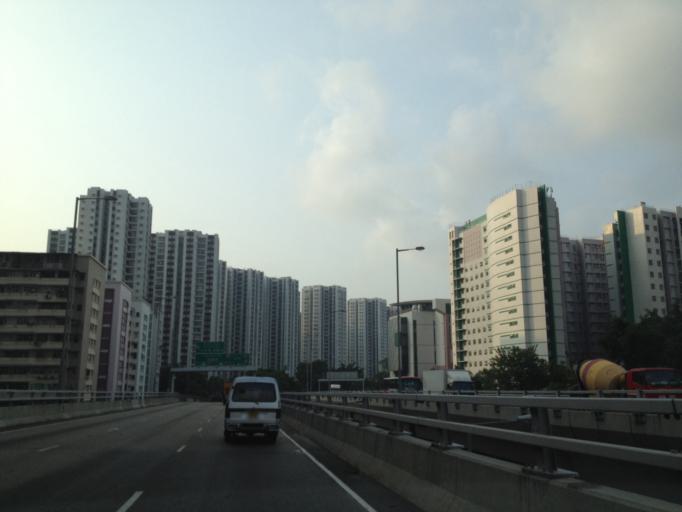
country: HK
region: Wanchai
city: Wan Chai
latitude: 22.2828
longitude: 114.2229
